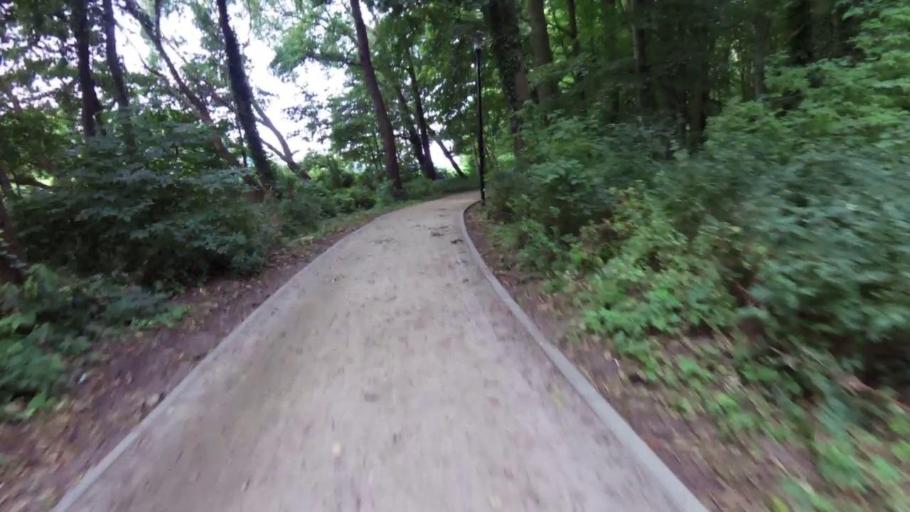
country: PL
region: West Pomeranian Voivodeship
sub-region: Powiat choszczenski
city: Choszczno
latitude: 53.1579
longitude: 15.4290
